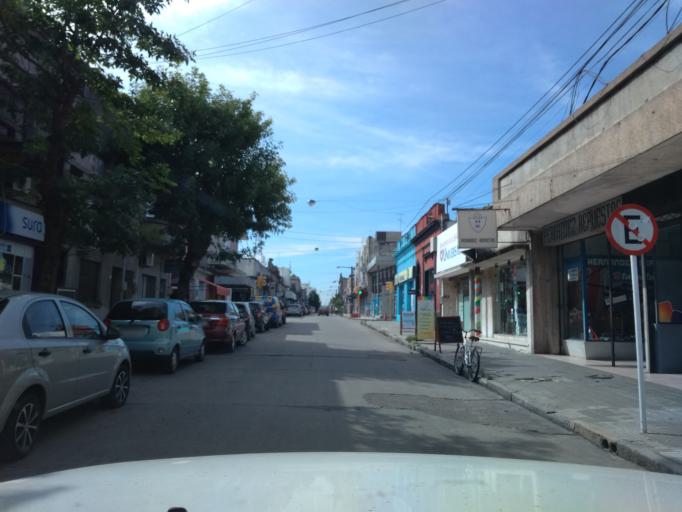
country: UY
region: Florida
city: Florida
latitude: -34.0961
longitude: -56.2182
